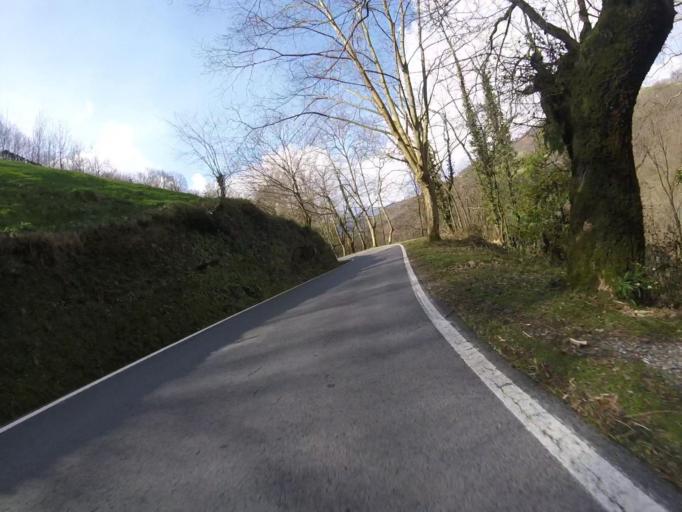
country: ES
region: Navarre
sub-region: Provincia de Navarra
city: Etxalar
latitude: 43.2485
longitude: -1.6147
